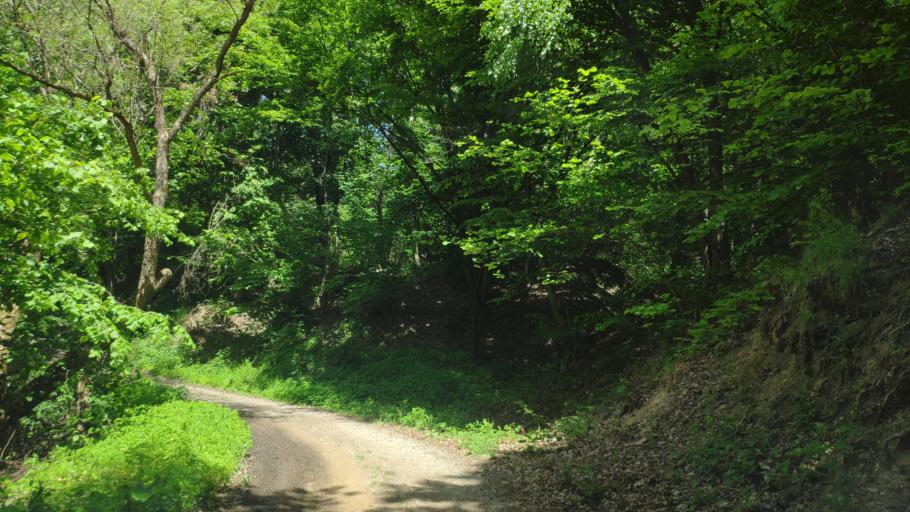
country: SK
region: Kosicky
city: Medzev
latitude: 48.7214
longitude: 20.9649
